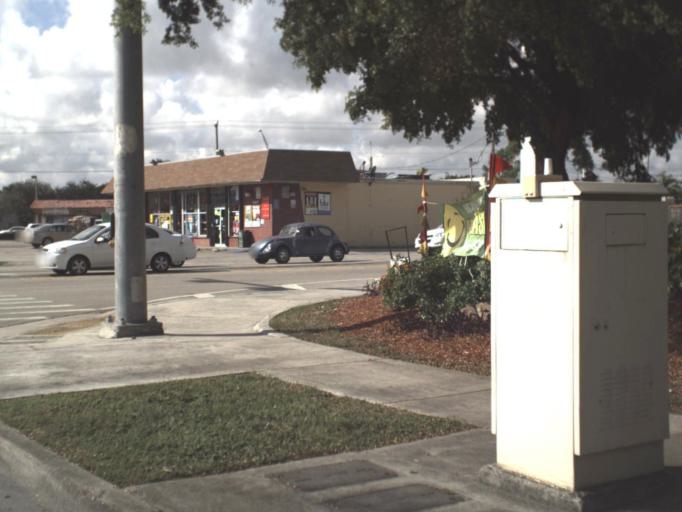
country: US
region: Florida
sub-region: Miami-Dade County
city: Leisure City
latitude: 25.4994
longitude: -80.4446
